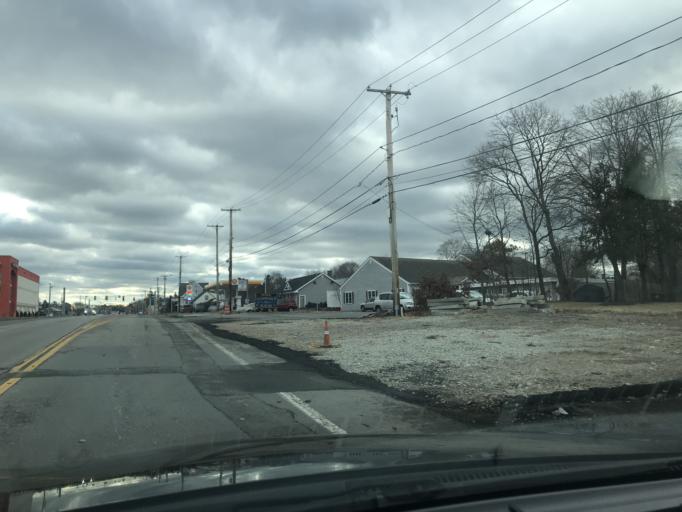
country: US
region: Massachusetts
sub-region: Plymouth County
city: Rockland
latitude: 42.1552
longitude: -70.9552
